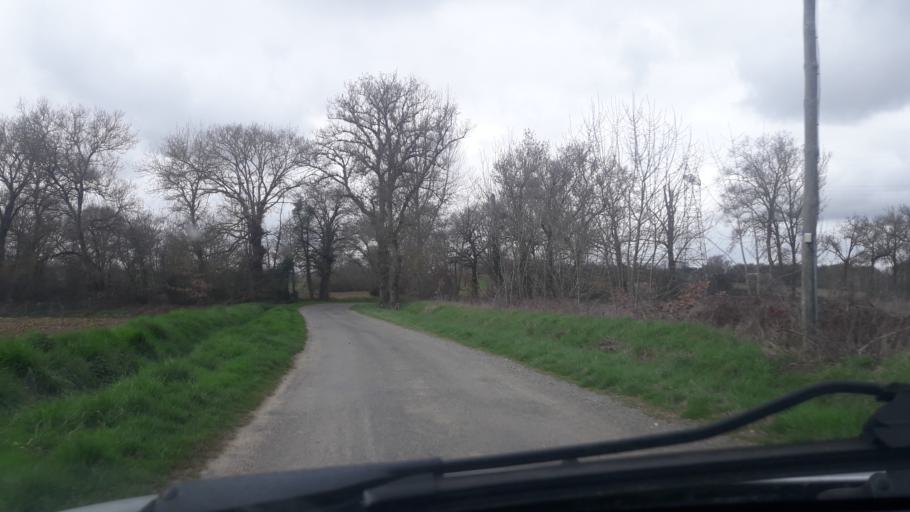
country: FR
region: Midi-Pyrenees
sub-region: Departement du Gers
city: Pujaudran
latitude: 43.6362
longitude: 1.0444
